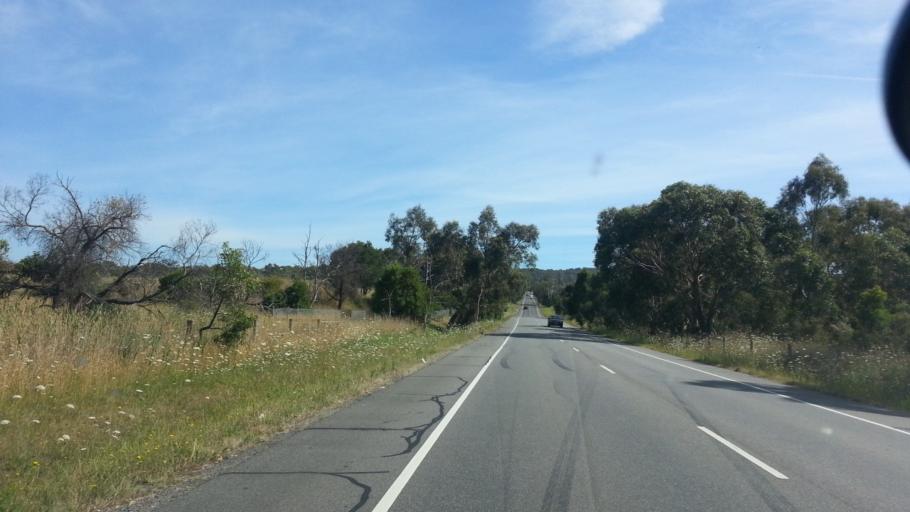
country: AU
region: Victoria
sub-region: Casey
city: Endeavour Hills
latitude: -37.9610
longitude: 145.2491
